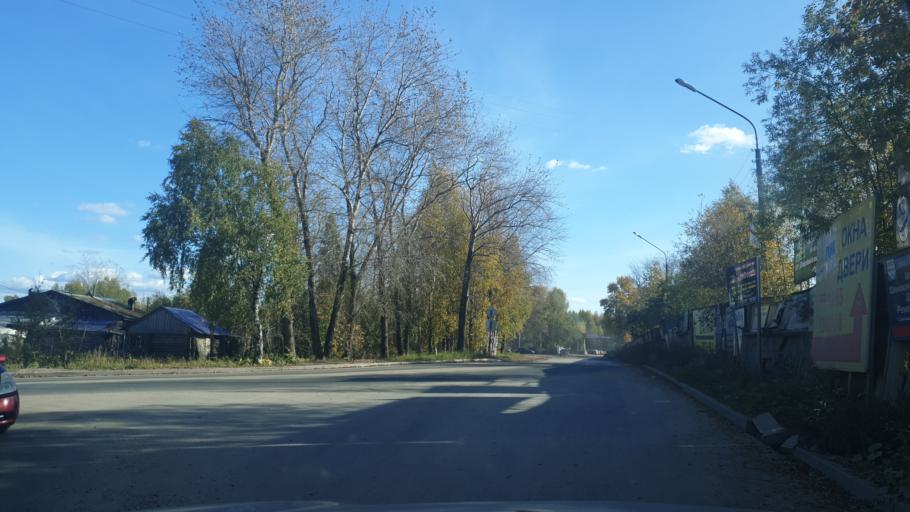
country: RU
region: Komi Republic
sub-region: Syktyvdinskiy Rayon
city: Syktyvkar
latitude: 61.6848
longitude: 50.7951
